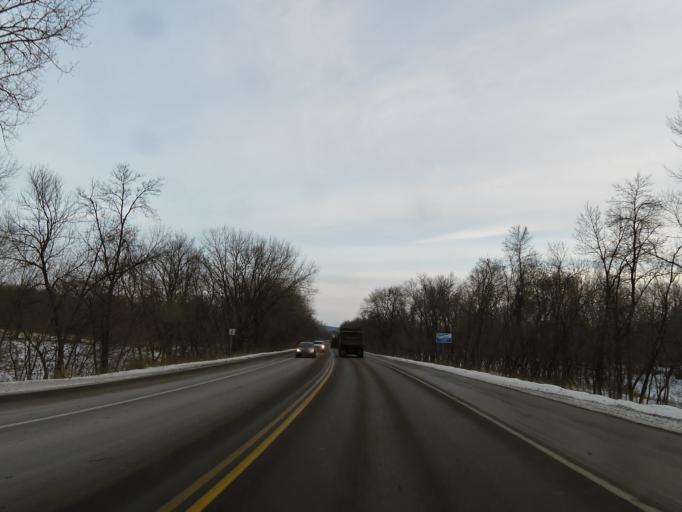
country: US
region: Minnesota
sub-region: Carver County
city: Chaska
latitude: 44.7806
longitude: -93.5978
